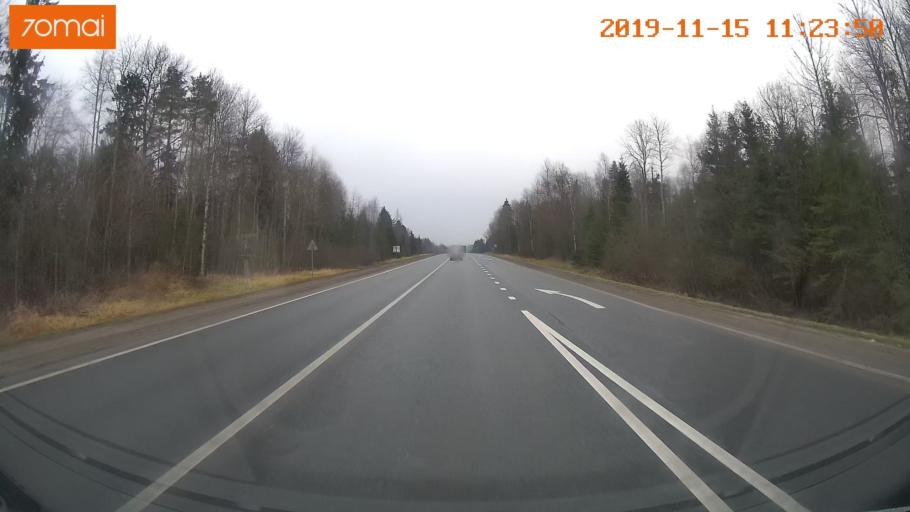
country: RU
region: Vologda
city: Molochnoye
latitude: 59.1538
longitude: 39.3914
